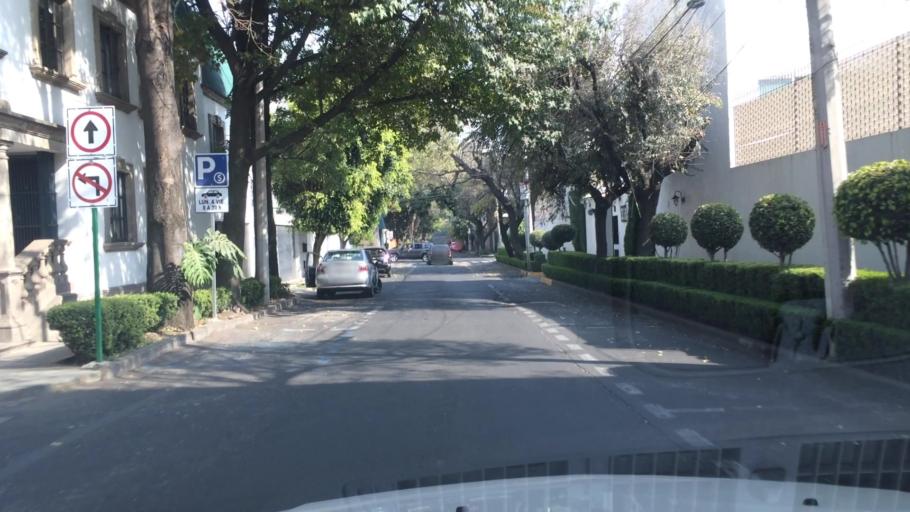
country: MX
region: Mexico City
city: Coyoacan
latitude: 19.3619
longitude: -99.1780
